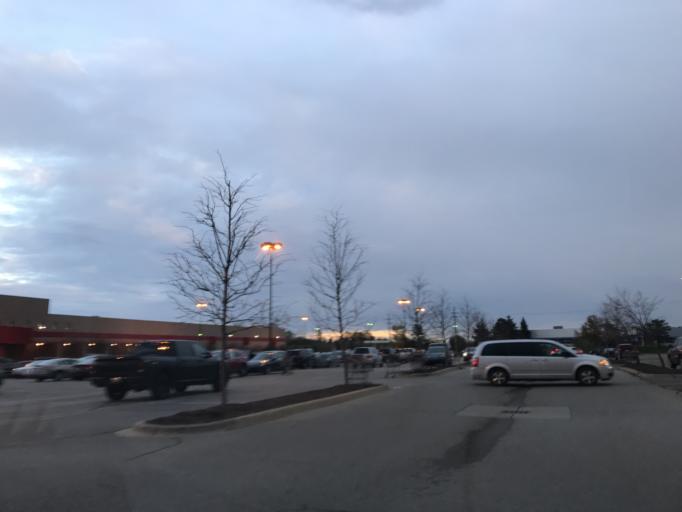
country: US
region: Michigan
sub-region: Wayne County
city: Northville
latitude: 42.4331
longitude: -83.4318
